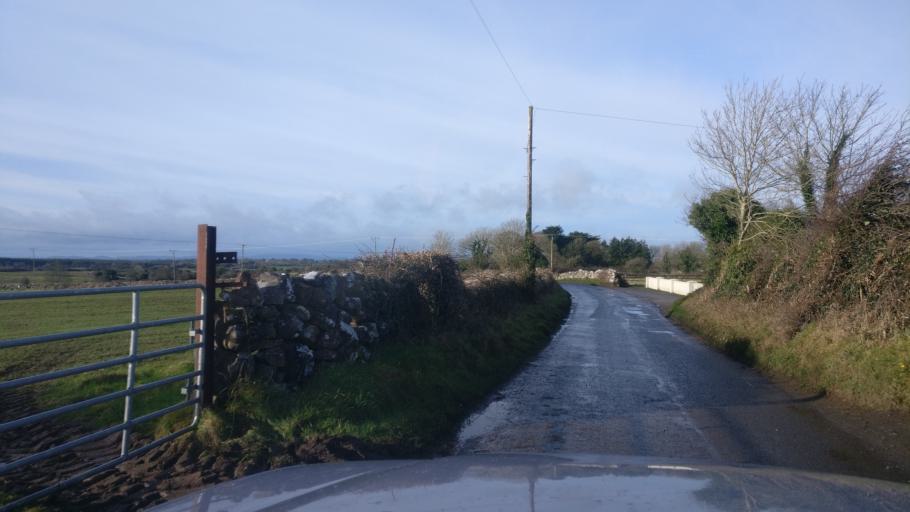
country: IE
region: Connaught
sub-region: County Galway
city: Loughrea
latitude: 53.1958
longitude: -8.6261
